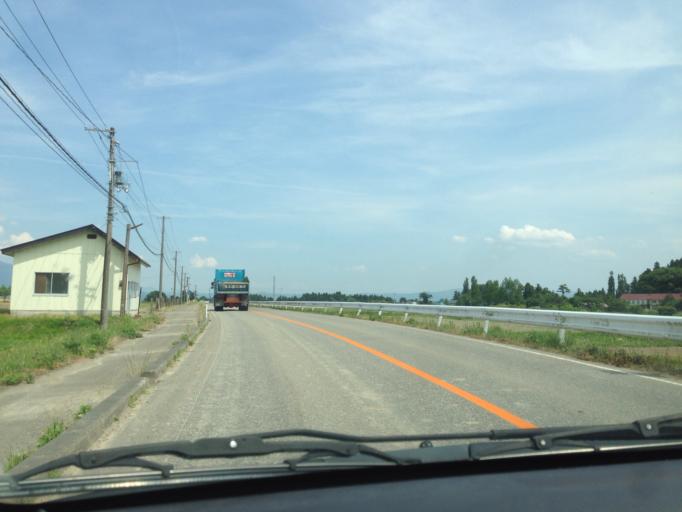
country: JP
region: Fukushima
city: Kitakata
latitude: 37.6059
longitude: 139.8071
